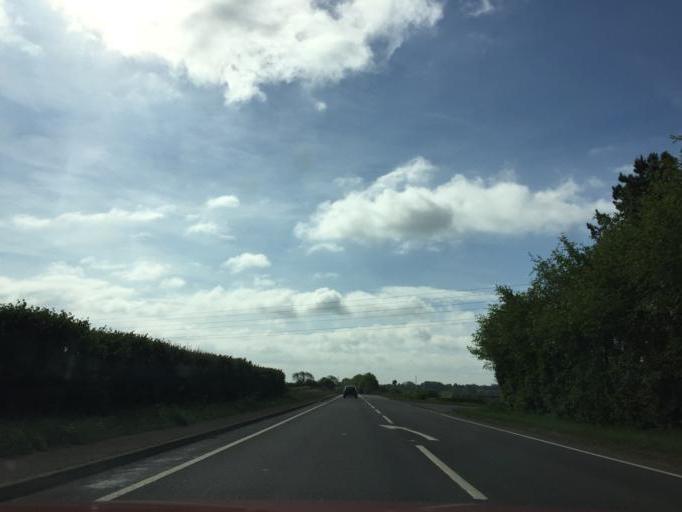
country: GB
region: England
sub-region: Northamptonshire
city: Towcester
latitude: 52.1166
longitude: -0.9617
